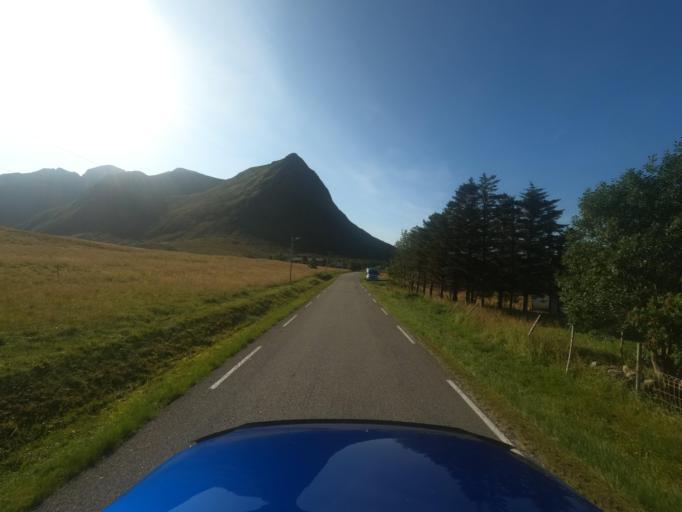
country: NO
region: Nordland
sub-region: Vestvagoy
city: Evjen
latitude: 68.3244
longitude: 13.9189
